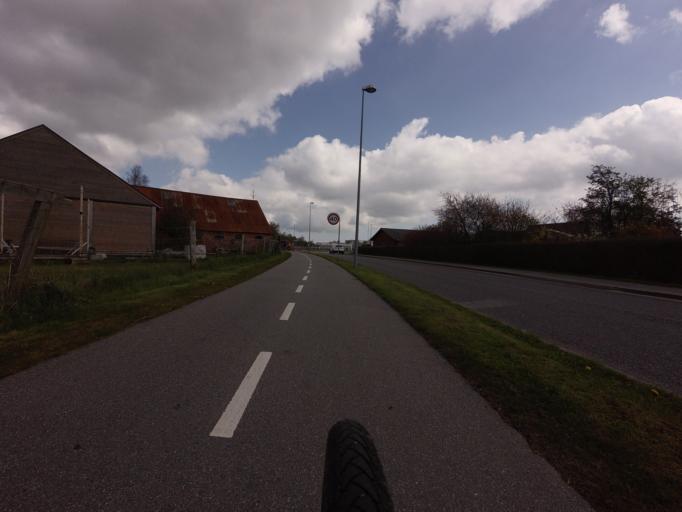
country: DK
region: North Denmark
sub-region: Mariagerfjord Kommune
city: Hadsund
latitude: 56.7214
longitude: 10.1280
